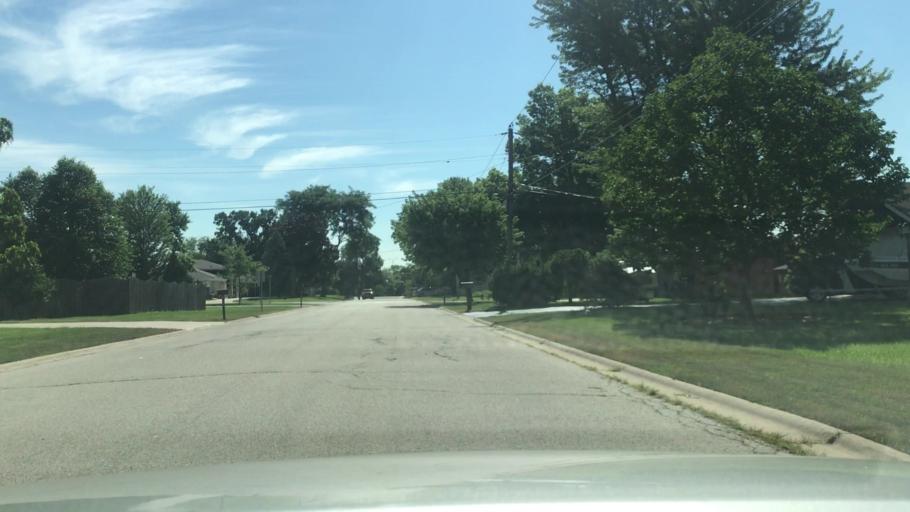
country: US
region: Illinois
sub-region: Cook County
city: Hickory Hills
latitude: 41.7366
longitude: -87.8272
